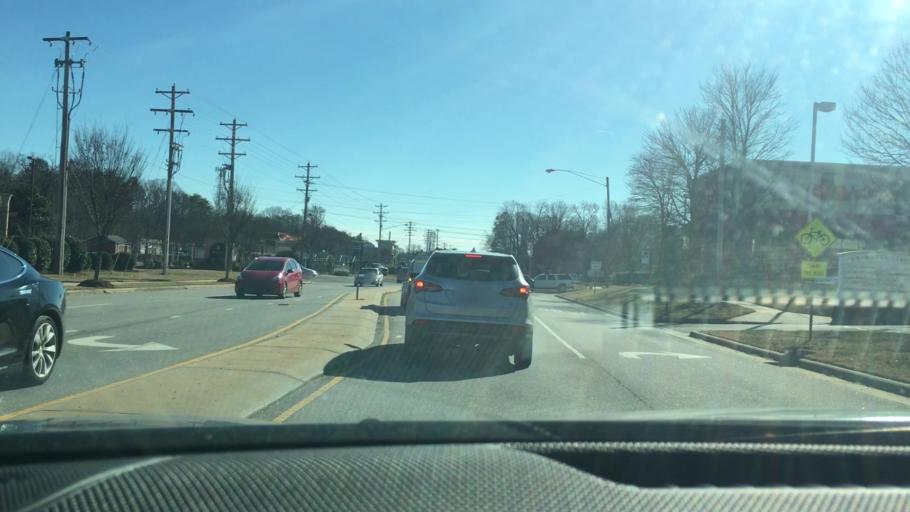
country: US
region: North Carolina
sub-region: Mecklenburg County
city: Cornelius
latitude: 35.4763
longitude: -80.8915
